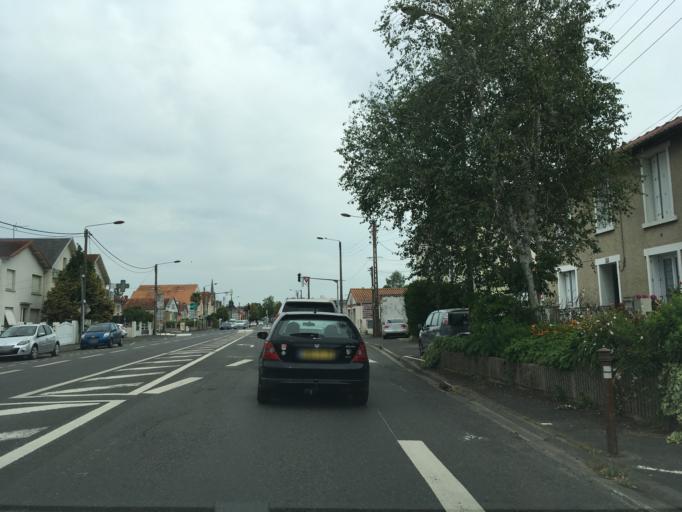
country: FR
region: Poitou-Charentes
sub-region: Departement des Deux-Sevres
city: Niort
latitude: 46.3146
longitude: -0.4752
